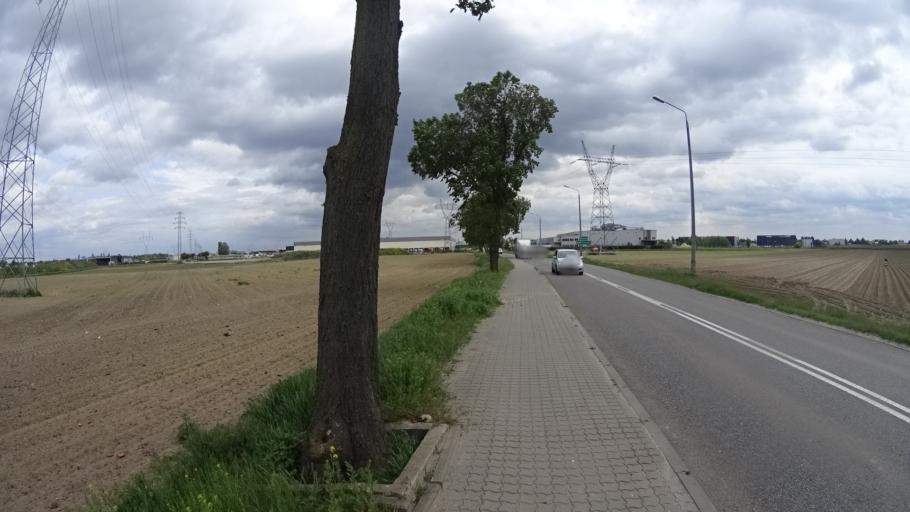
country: PL
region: Masovian Voivodeship
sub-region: Powiat warszawski zachodni
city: Babice
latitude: 52.2230
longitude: 20.8337
